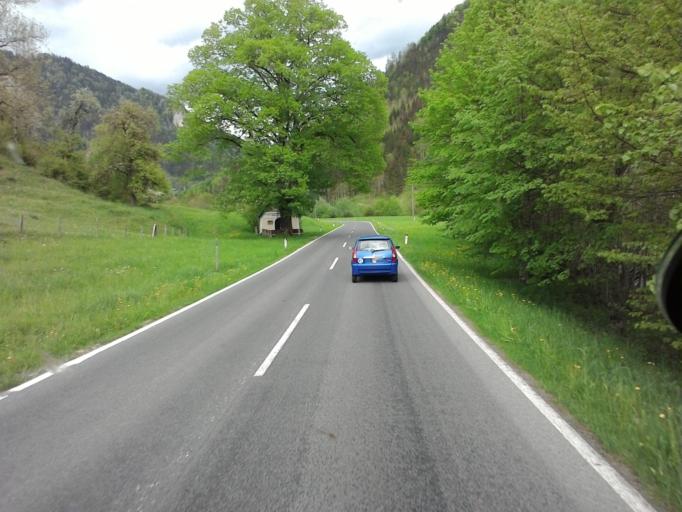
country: AT
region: Styria
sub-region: Politischer Bezirk Liezen
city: Altenmarkt bei Sankt Gallen
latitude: 47.7244
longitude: 14.5935
